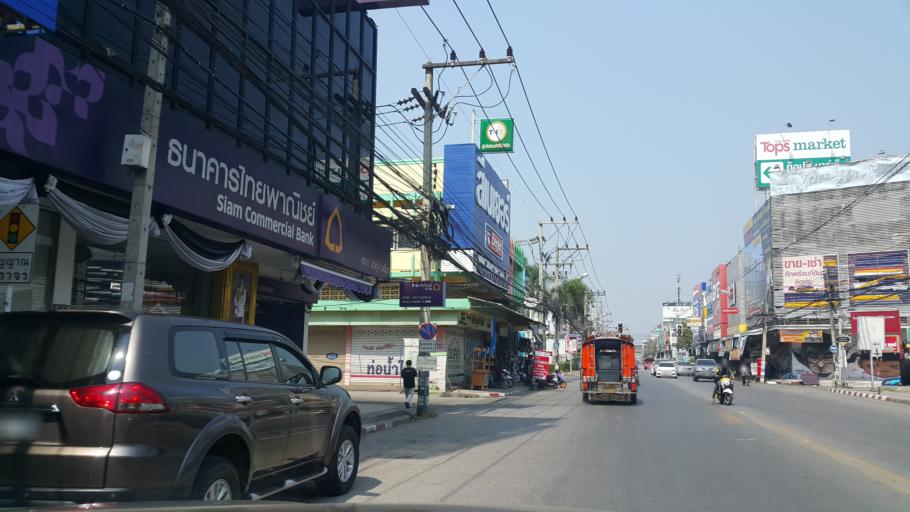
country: TH
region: Chiang Mai
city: Chiang Mai
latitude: 18.8014
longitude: 98.9858
